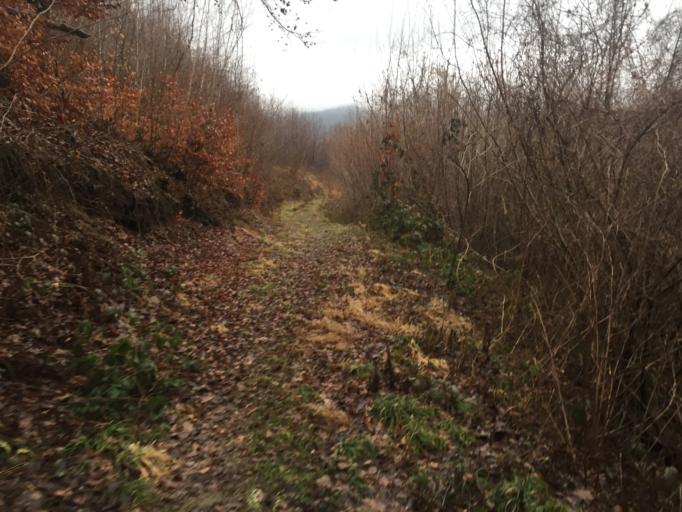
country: IT
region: Friuli Venezia Giulia
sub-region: Provincia di Udine
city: Cras
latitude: 46.1533
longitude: 13.6401
